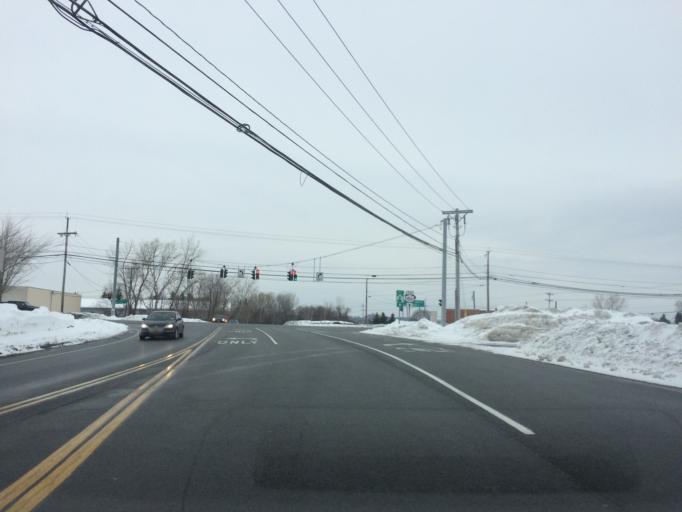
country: US
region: New York
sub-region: Monroe County
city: Rochester
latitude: 43.0940
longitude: -77.6136
